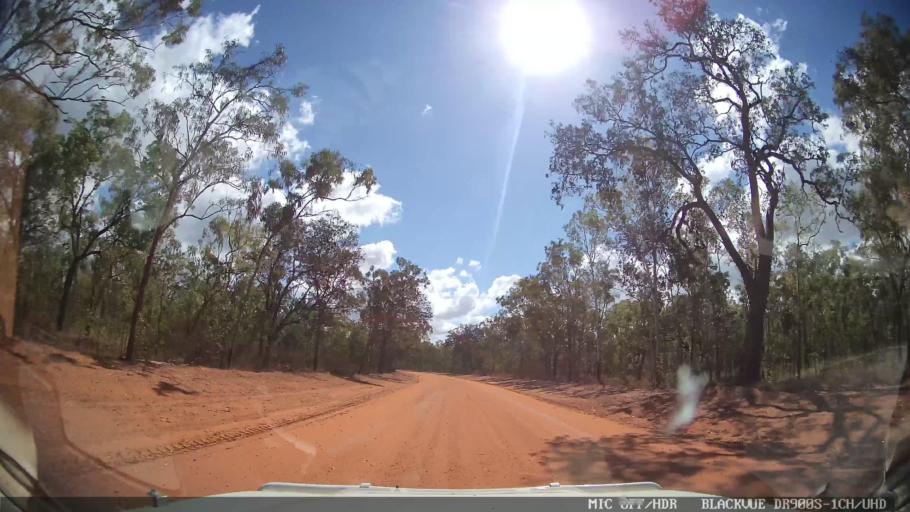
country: AU
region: Queensland
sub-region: Cook
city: Cooktown
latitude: -15.1920
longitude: 144.3737
